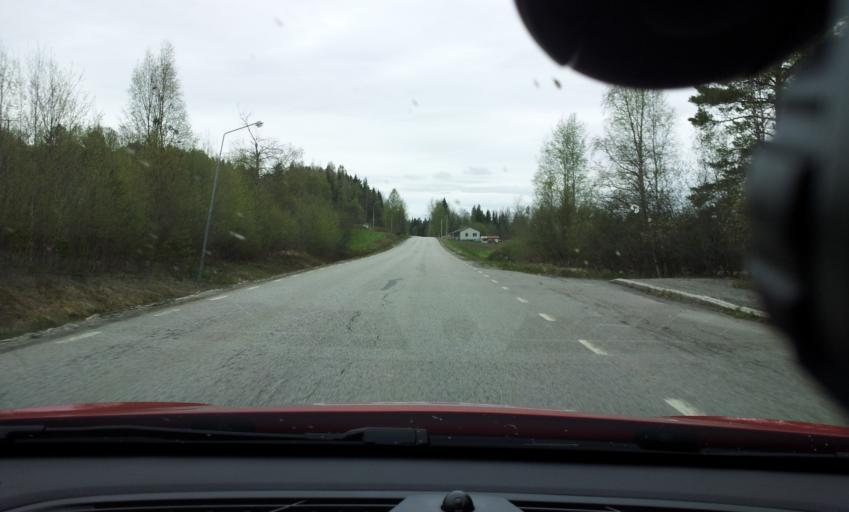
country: SE
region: Jaemtland
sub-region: Bergs Kommun
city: Hoverberg
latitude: 62.7226
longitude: 14.6007
